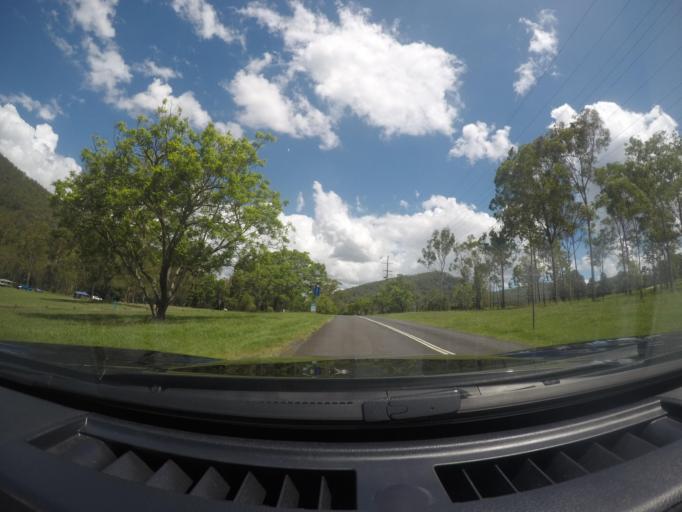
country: AU
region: Queensland
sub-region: Moreton Bay
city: Woodford
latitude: -27.1206
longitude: 152.5503
